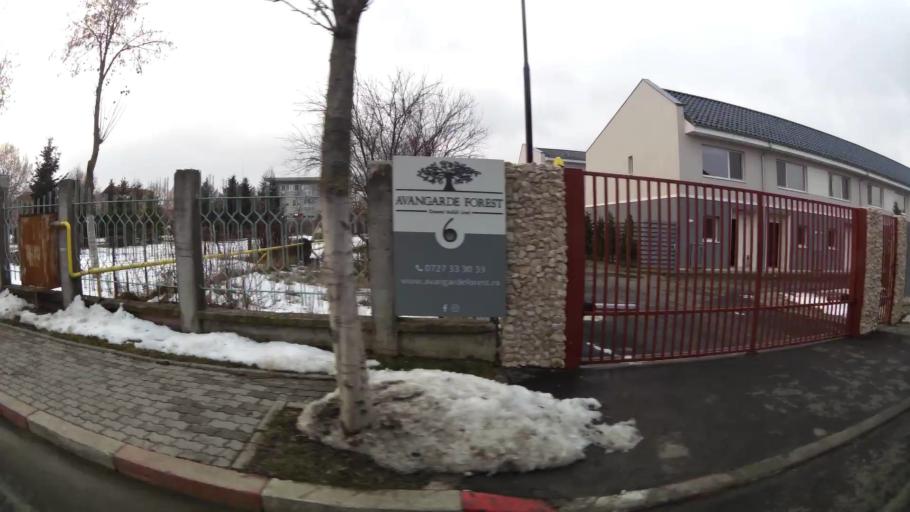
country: RO
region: Ilfov
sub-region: Voluntari City
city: Voluntari
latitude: 44.4975
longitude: 26.1688
